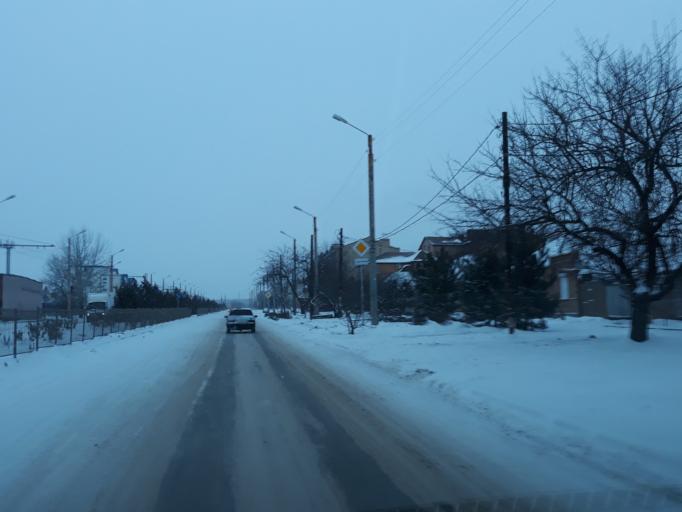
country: RU
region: Rostov
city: Taganrog
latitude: 47.2726
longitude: 38.9193
